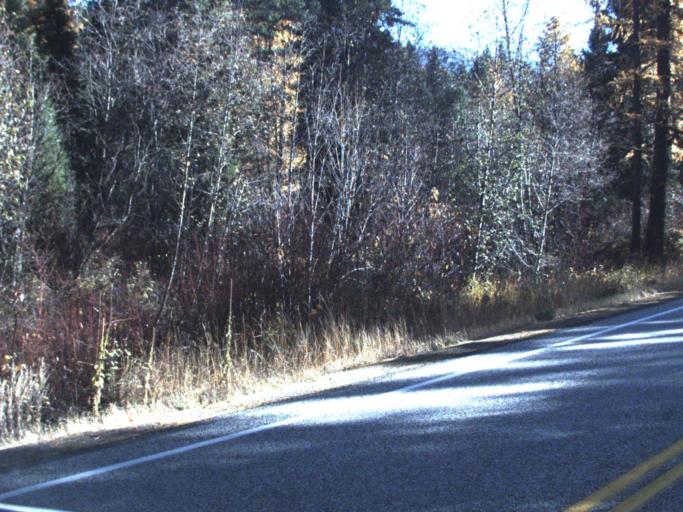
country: US
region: Washington
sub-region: Ferry County
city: Republic
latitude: 48.5992
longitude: -118.6515
